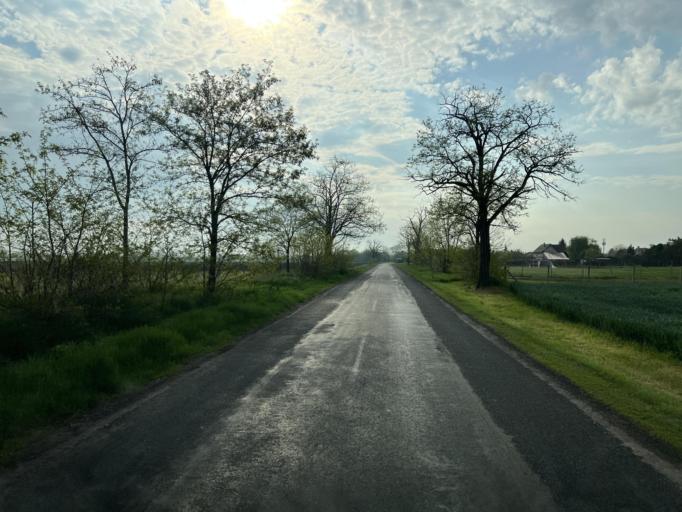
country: HU
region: Pest
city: Cegledbercel
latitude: 47.2144
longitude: 19.7163
